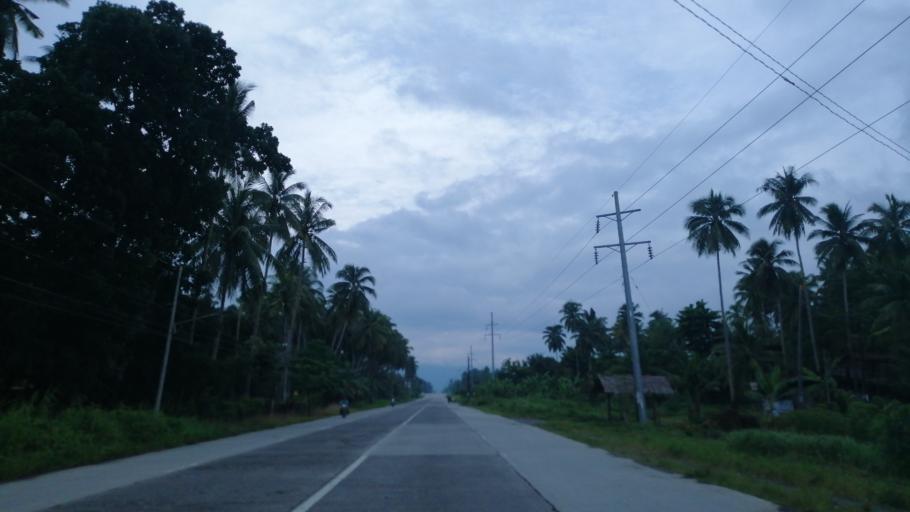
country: PH
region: Davao
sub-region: Province of Davao del Norte
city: Corocotan
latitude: 7.3974
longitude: 125.7771
